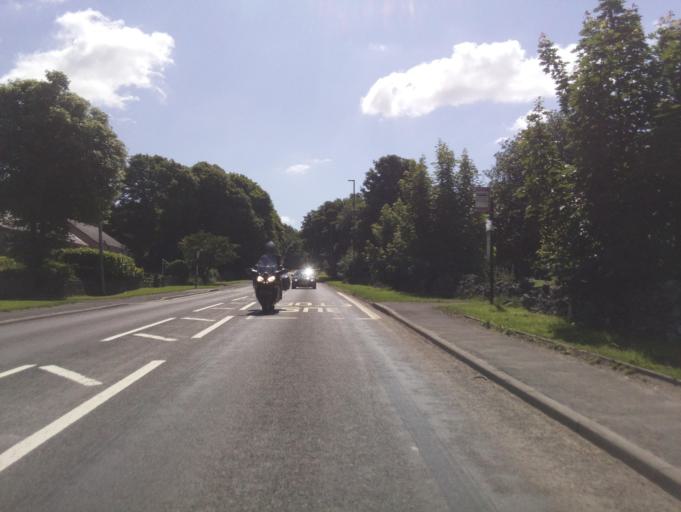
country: GB
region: England
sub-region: Derbyshire
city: Buxton
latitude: 53.2460
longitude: -1.9032
